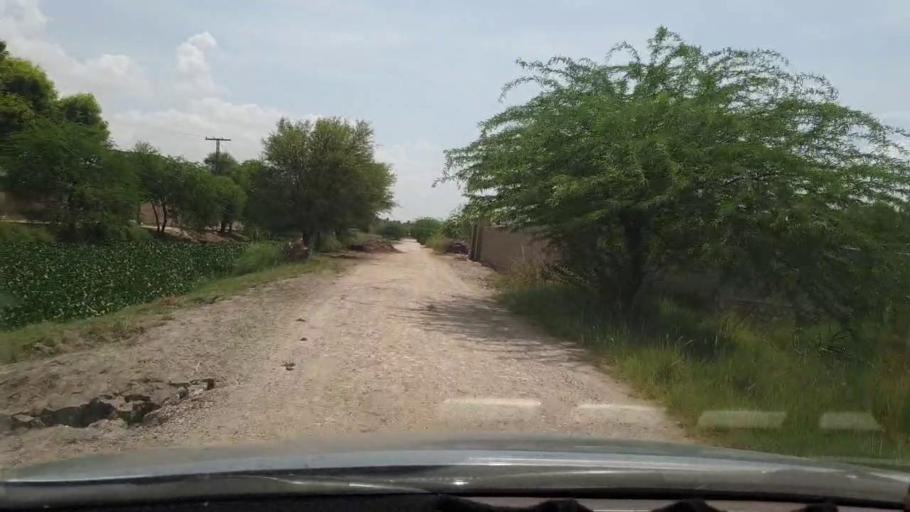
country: PK
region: Sindh
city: Khairpur
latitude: 27.4674
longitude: 68.7964
